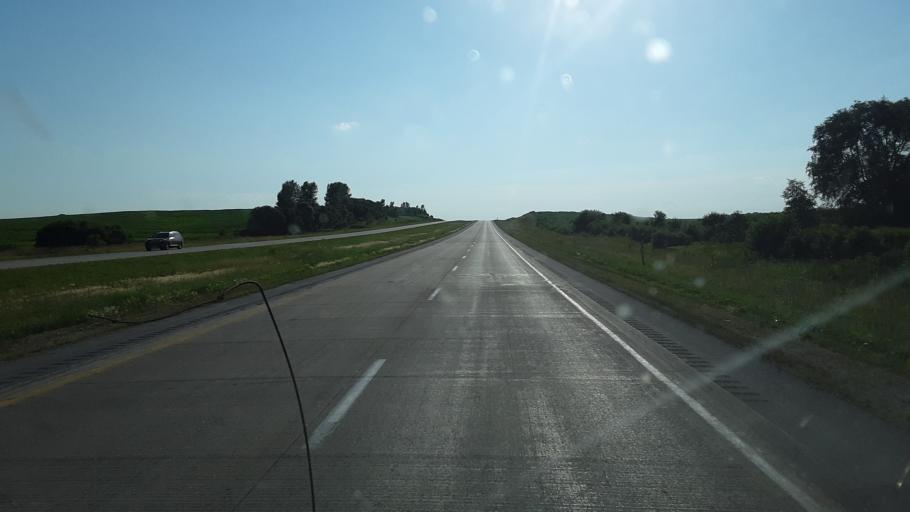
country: US
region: Iowa
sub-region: Hardin County
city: Iowa Falls
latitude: 42.4483
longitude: -93.3089
